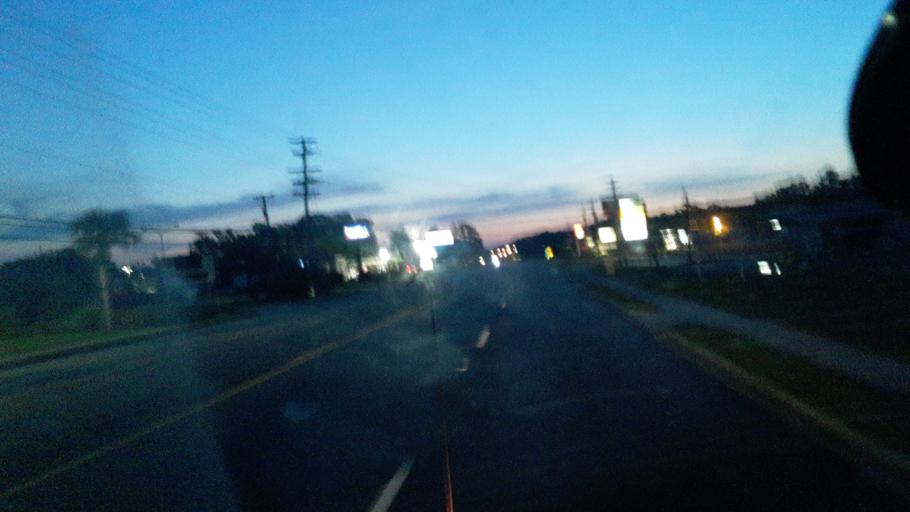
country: US
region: South Carolina
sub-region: Horry County
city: Little River
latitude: 33.8768
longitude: -78.6130
